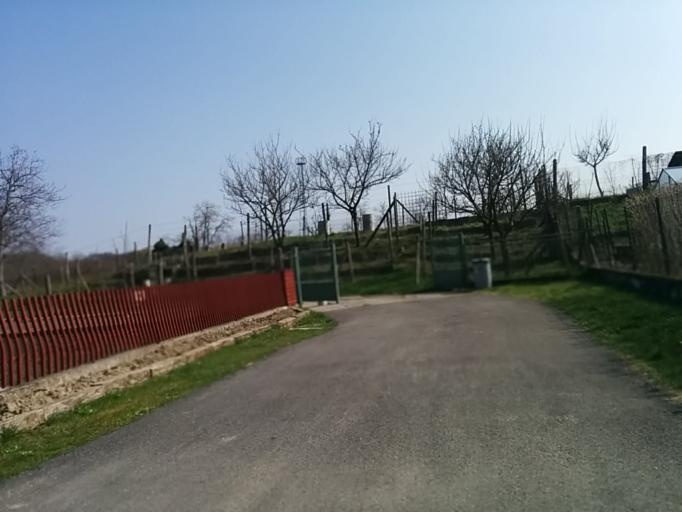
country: SK
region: Trnavsky
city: Sladkovicovo
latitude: 48.2456
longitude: 17.6229
